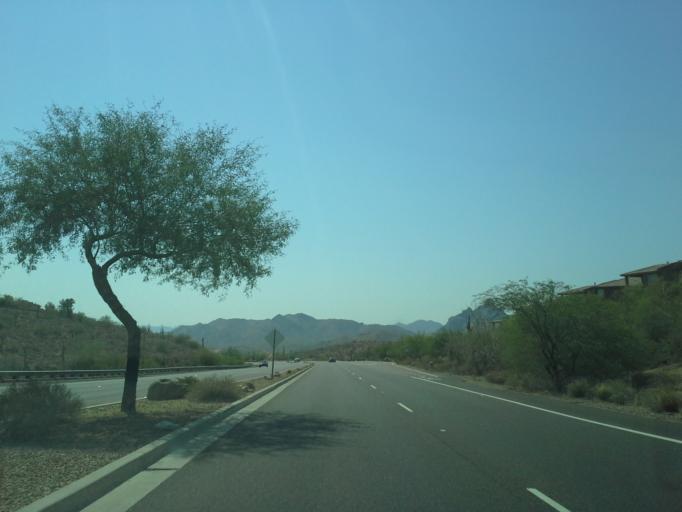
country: US
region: Arizona
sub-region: Maricopa County
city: Fountain Hills
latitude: 33.5802
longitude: -111.7302
